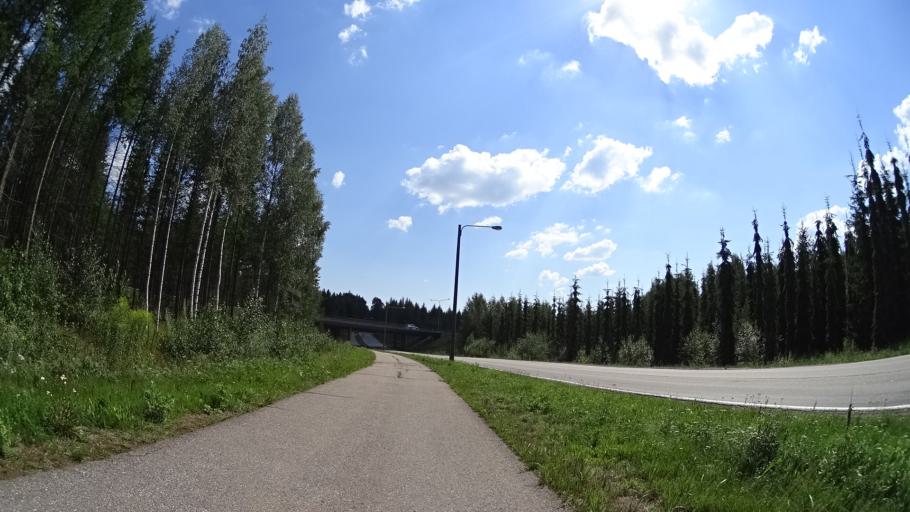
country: FI
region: Uusimaa
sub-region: Helsinki
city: Tuusula
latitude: 60.3503
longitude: 24.9983
